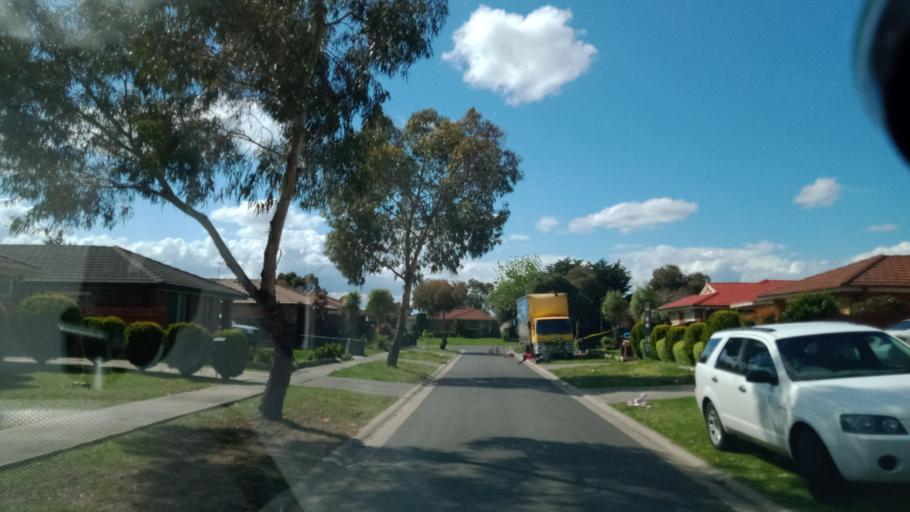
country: AU
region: Victoria
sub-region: Casey
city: Cranbourne West
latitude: -38.0981
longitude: 145.2599
